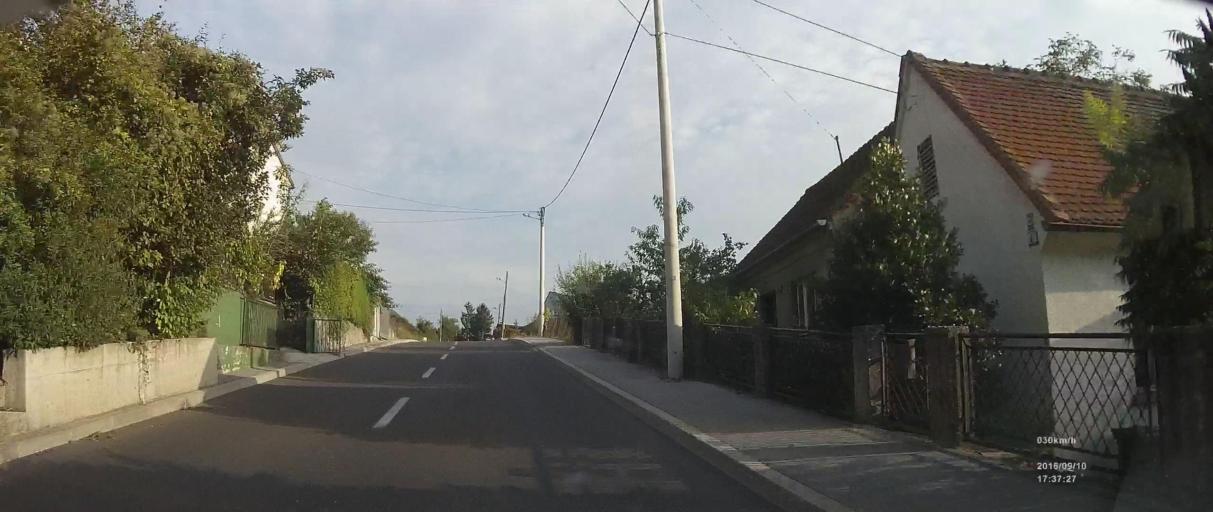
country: HR
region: Grad Zagreb
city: Zagreb
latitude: 45.8521
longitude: 15.9359
